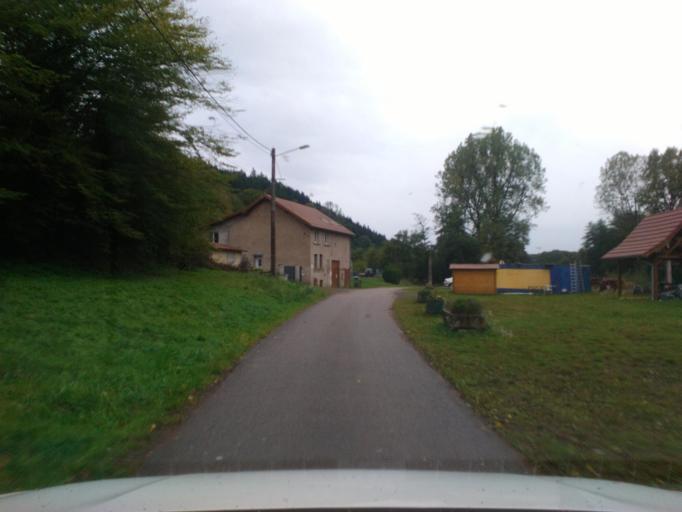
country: FR
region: Lorraine
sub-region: Departement des Vosges
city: Senones
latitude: 48.4211
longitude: 7.0116
